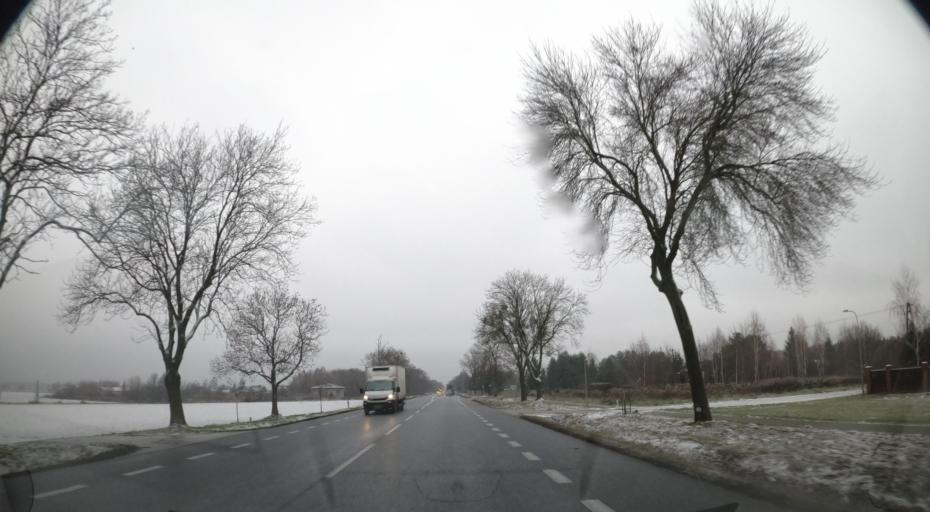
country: PL
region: Masovian Voivodeship
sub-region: Powiat sochaczewski
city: Sochaczew
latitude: 52.2242
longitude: 20.2963
